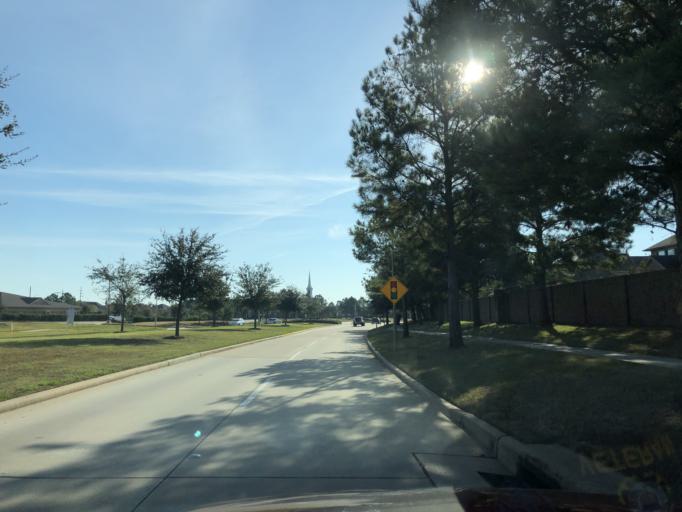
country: US
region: Texas
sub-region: Harris County
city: Tomball
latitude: 30.0543
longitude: -95.5702
